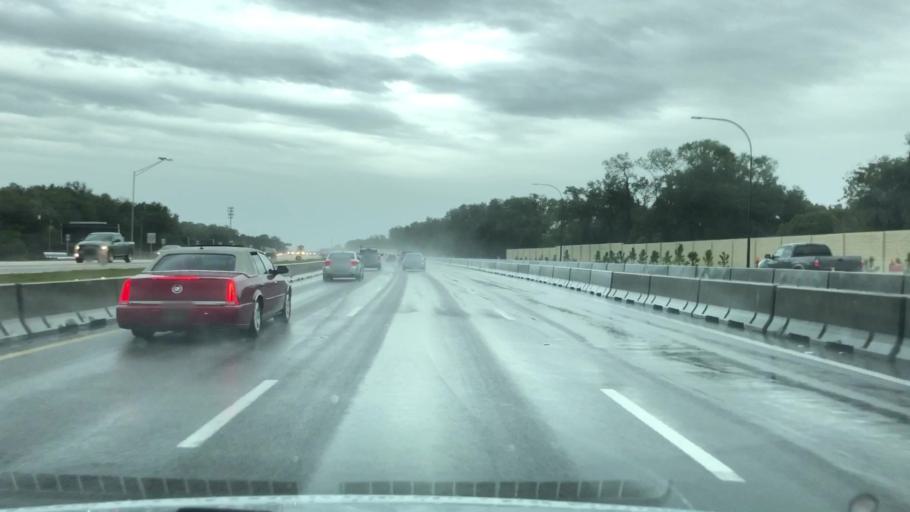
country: US
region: Florida
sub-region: Seminole County
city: Wekiwa Springs
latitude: 28.7045
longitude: -81.3829
